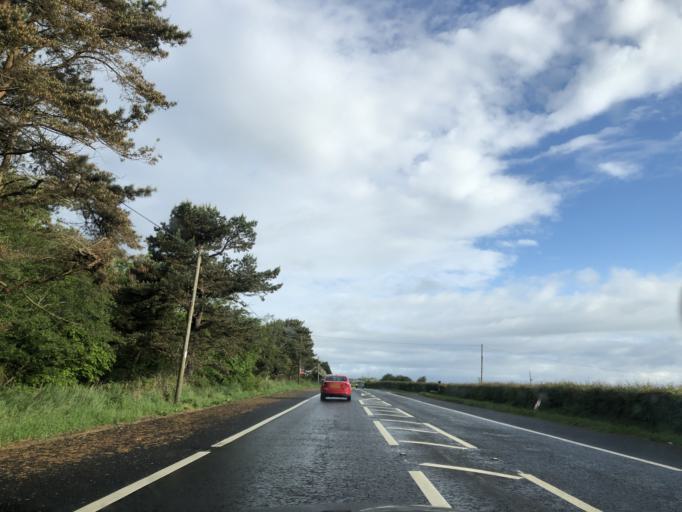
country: GB
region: Northern Ireland
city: Bushmills
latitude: 55.1518
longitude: -6.5710
